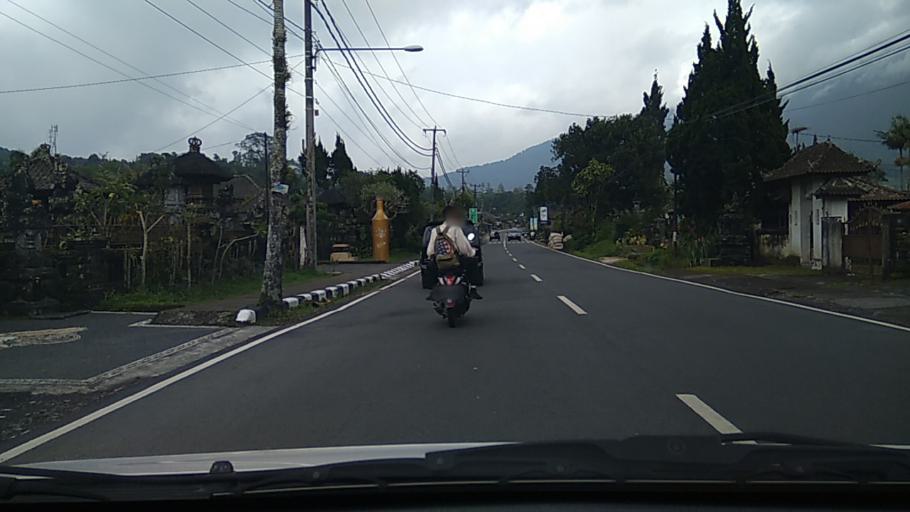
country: ID
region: Bali
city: Munduk
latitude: -8.2721
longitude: 115.1635
